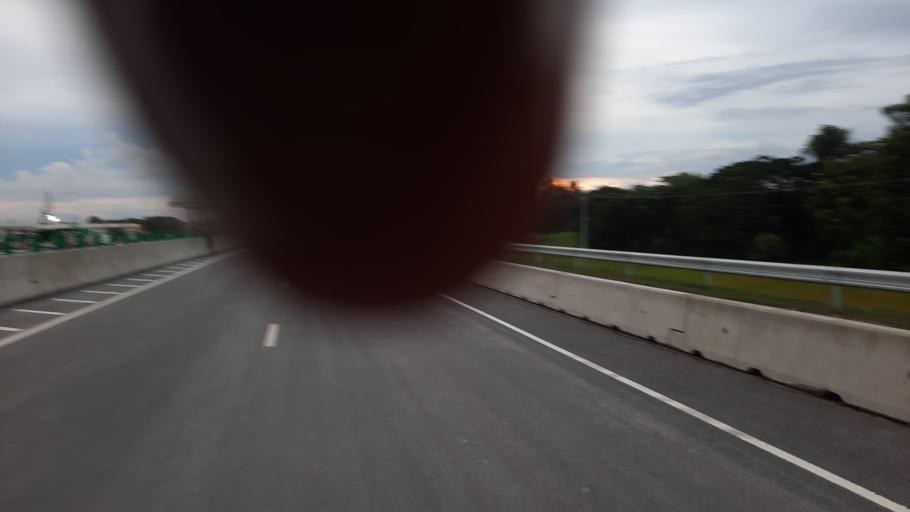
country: BD
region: Khulna
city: Kalia
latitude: 23.1909
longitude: 89.7015
